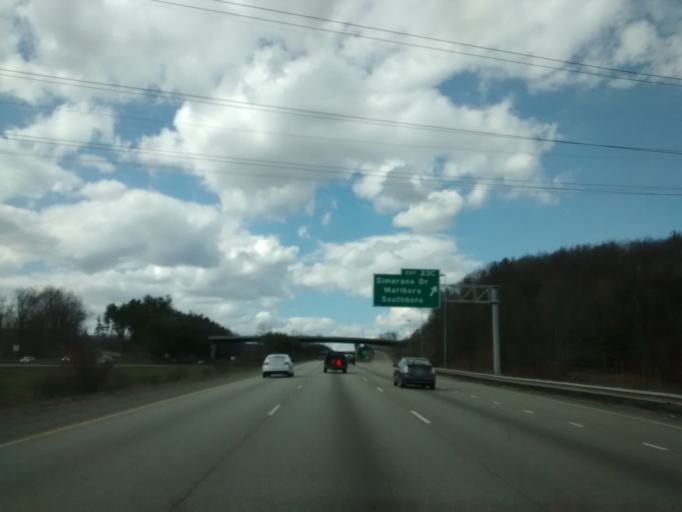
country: US
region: Massachusetts
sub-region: Middlesex County
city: Marlborough
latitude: 42.3171
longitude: -71.5693
